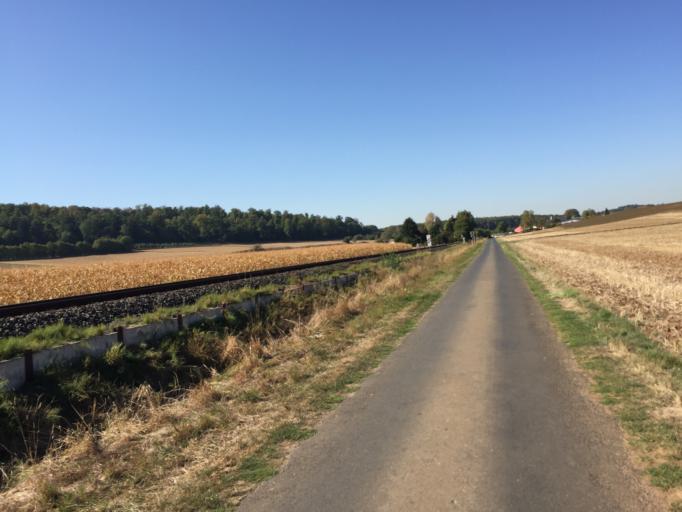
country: DE
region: Hesse
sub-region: Regierungsbezirk Darmstadt
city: Nidda
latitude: 50.4292
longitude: 8.9529
